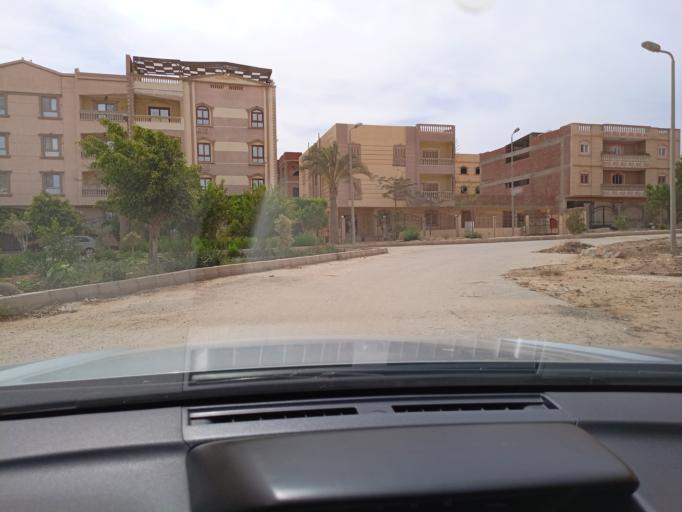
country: EG
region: Muhafazat al Qalyubiyah
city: Al Khankah
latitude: 30.2445
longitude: 31.4904
